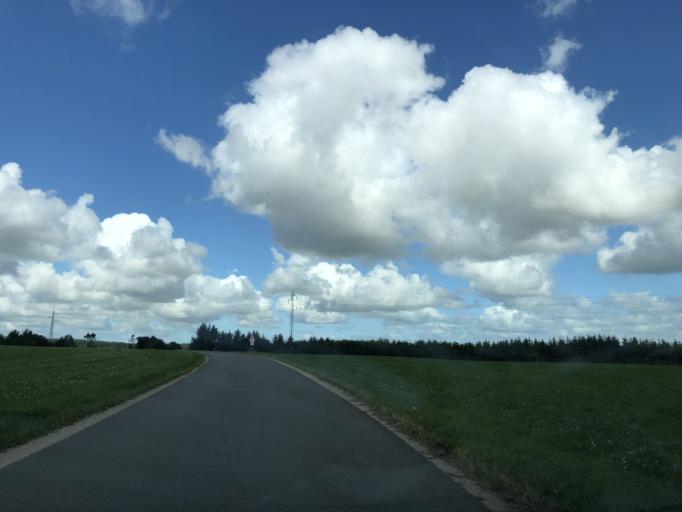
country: DK
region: Central Jutland
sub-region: Struer Kommune
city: Struer
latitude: 56.4779
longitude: 8.5324
